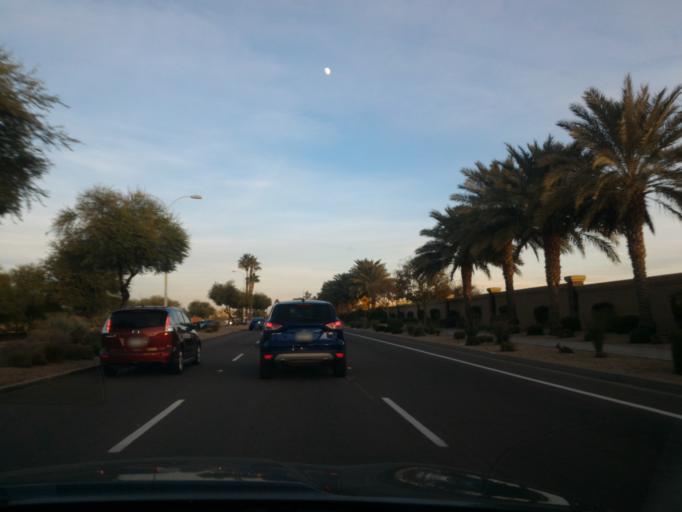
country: US
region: Arizona
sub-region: Maricopa County
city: Chandler
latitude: 33.3054
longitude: -111.9182
